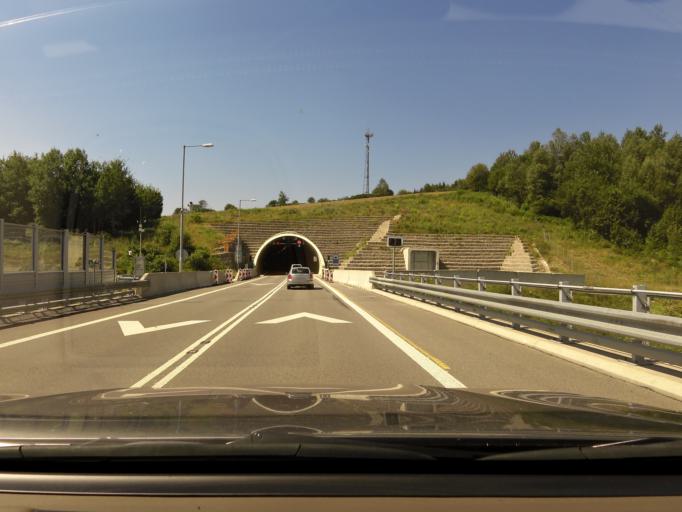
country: SK
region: Zilinsky
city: Cadca
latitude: 49.4896
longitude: 18.7971
